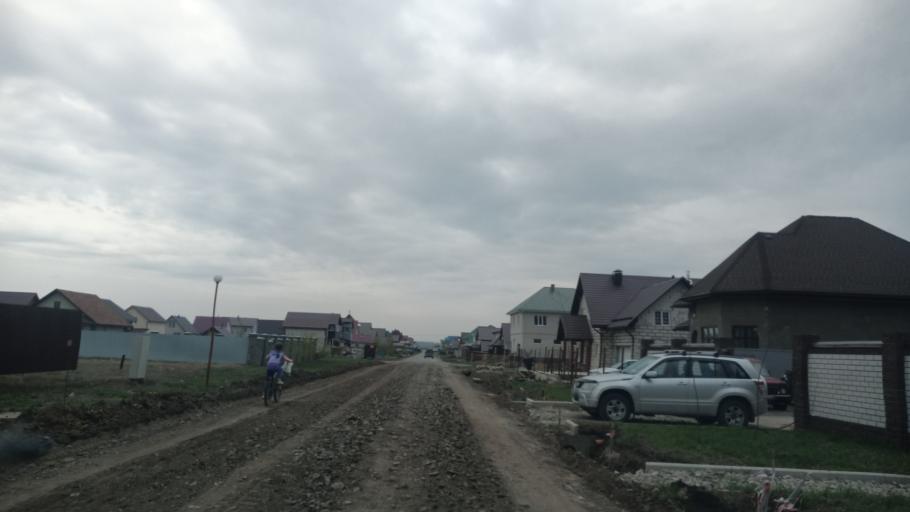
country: RU
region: Altai Krai
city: Yuzhnyy
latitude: 53.2259
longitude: 83.6909
